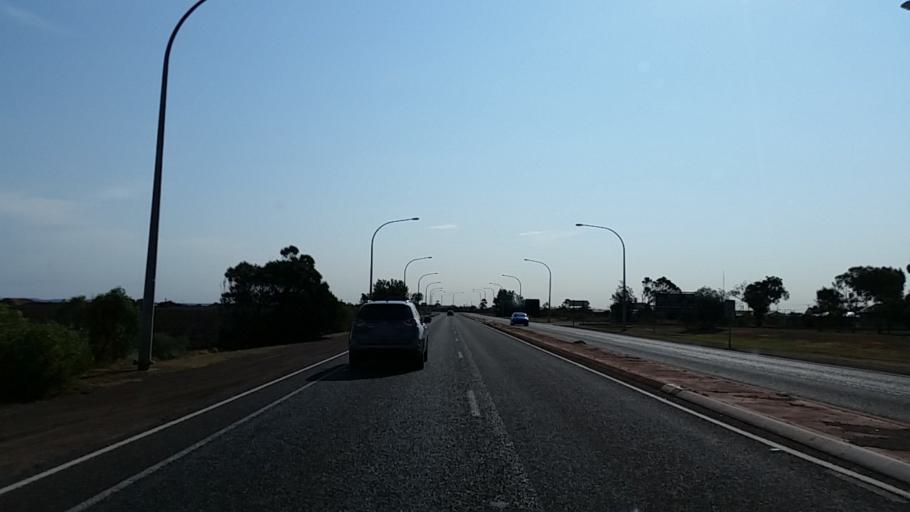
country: AU
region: South Australia
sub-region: Whyalla
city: Whyalla
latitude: -33.0402
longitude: 137.5603
